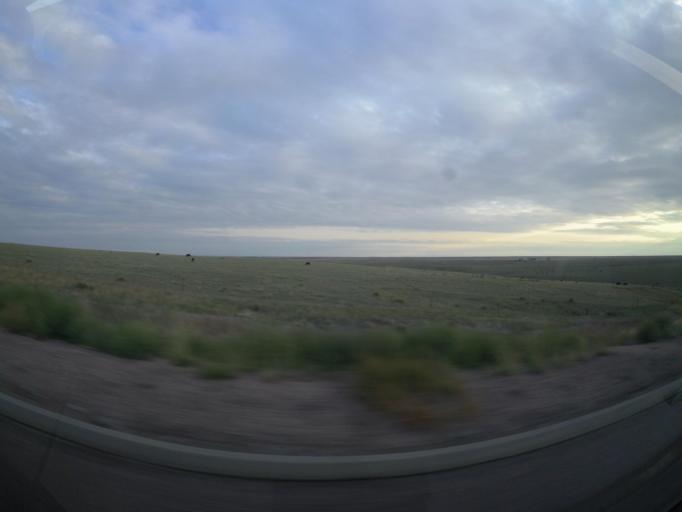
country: US
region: Kansas
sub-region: Cheyenne County
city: Saint Francis
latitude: 39.7469
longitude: -102.0682
